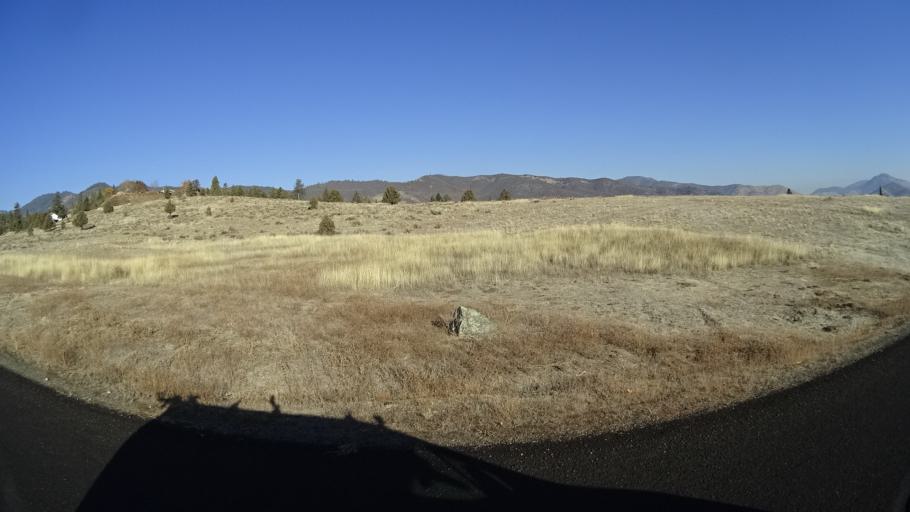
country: US
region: California
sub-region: Siskiyou County
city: Yreka
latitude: 41.7271
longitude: -122.6496
